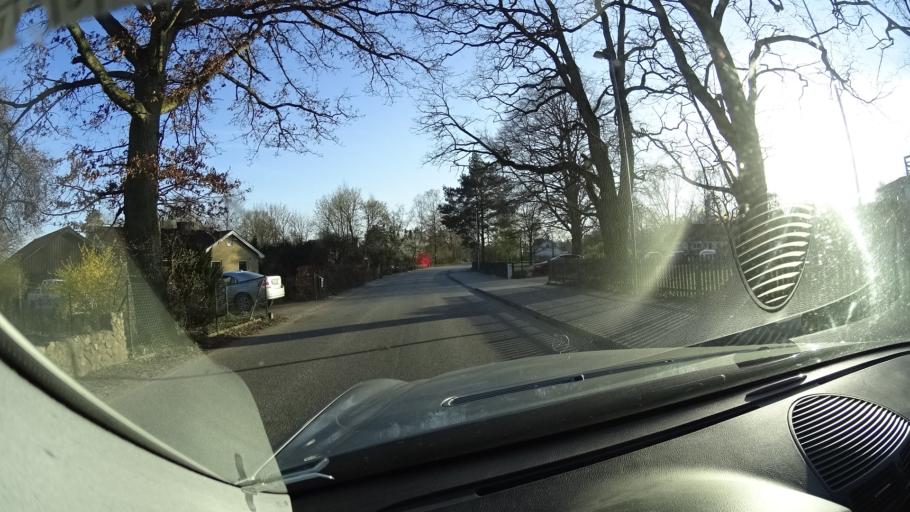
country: SE
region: Skane
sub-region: Hoors Kommun
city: Satofta
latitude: 55.9073
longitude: 13.5507
